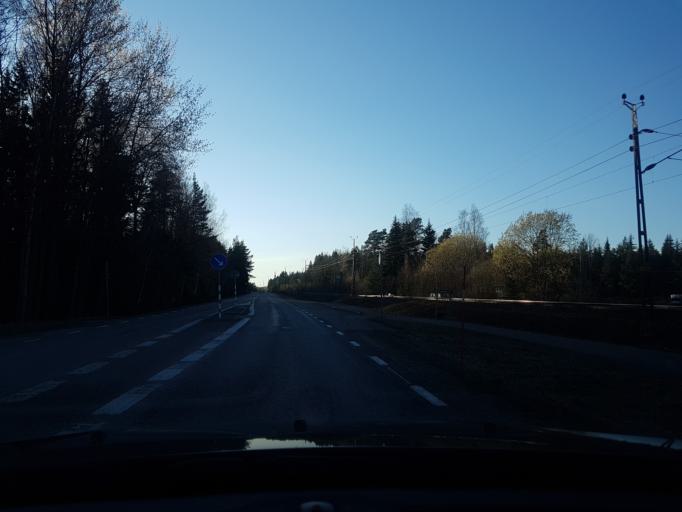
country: SE
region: Vaestmanland
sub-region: Sala Kommun
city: Sala
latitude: 59.9473
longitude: 16.5426
